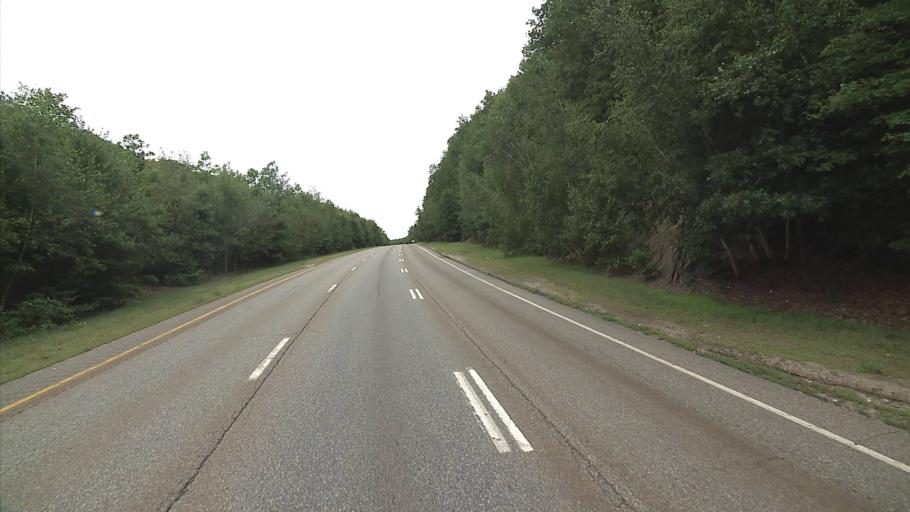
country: US
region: Connecticut
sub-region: Litchfield County
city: Thomaston
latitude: 41.7071
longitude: -73.0796
